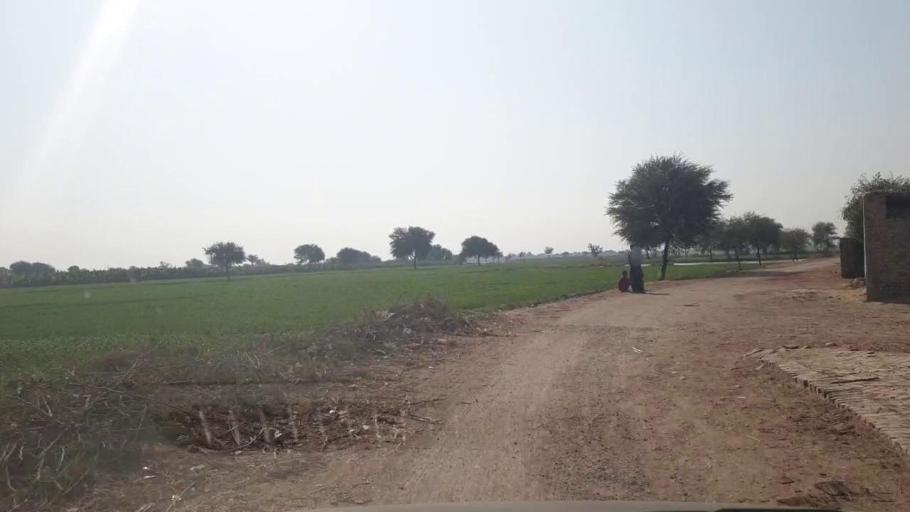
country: PK
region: Sindh
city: Tando Adam
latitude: 25.7497
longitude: 68.6148
